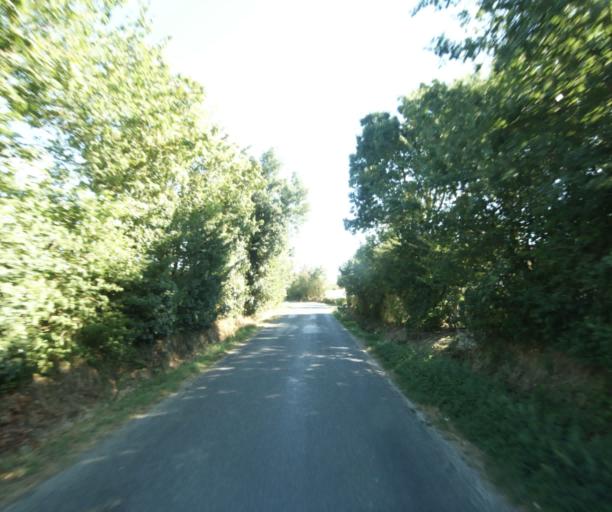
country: FR
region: Midi-Pyrenees
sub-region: Departement de la Haute-Garonne
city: Revel
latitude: 43.4990
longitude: 1.9453
